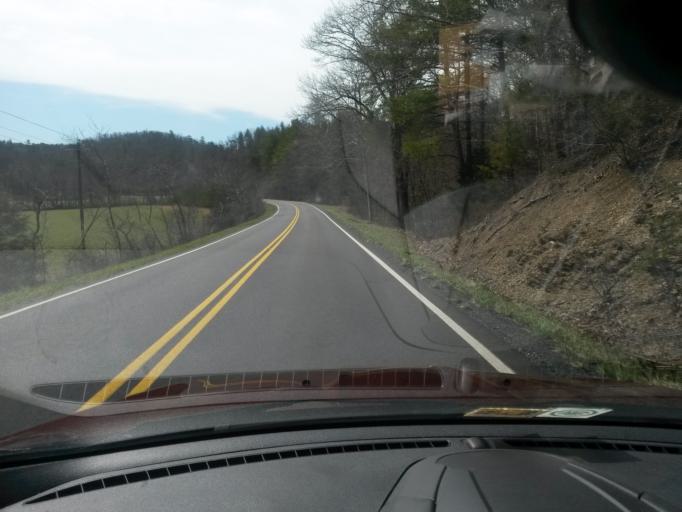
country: US
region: West Virginia
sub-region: Greenbrier County
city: White Sulphur Springs
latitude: 37.6835
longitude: -80.2300
